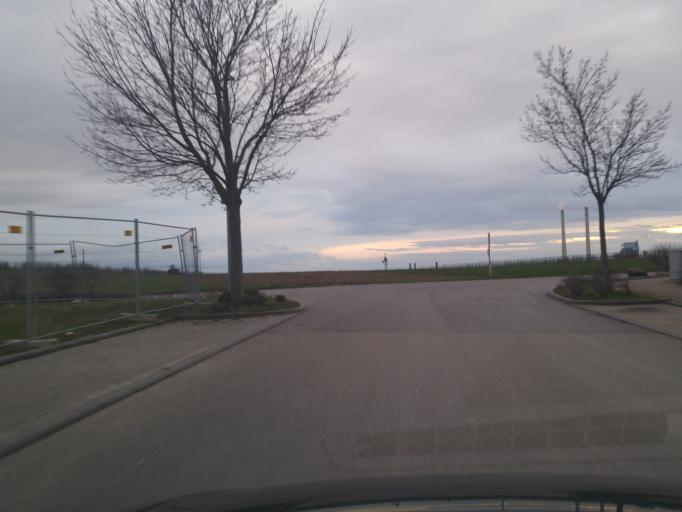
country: DE
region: Baden-Wuerttemberg
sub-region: Regierungsbezirk Stuttgart
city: Neckarsulm
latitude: 49.1803
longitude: 9.2394
